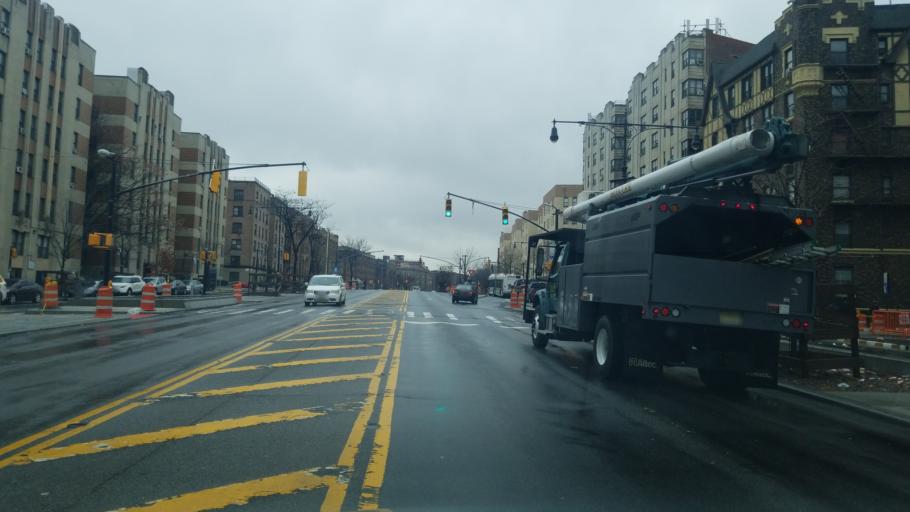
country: US
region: New York
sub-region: New York County
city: Inwood
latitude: 40.8420
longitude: -73.9124
